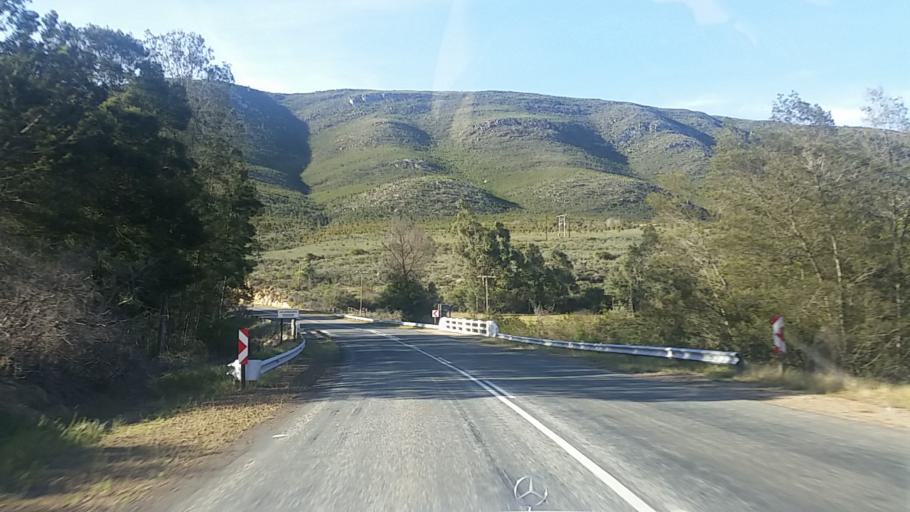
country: ZA
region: Western Cape
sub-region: Eden District Municipality
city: Knysna
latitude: -33.7631
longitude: 22.9628
